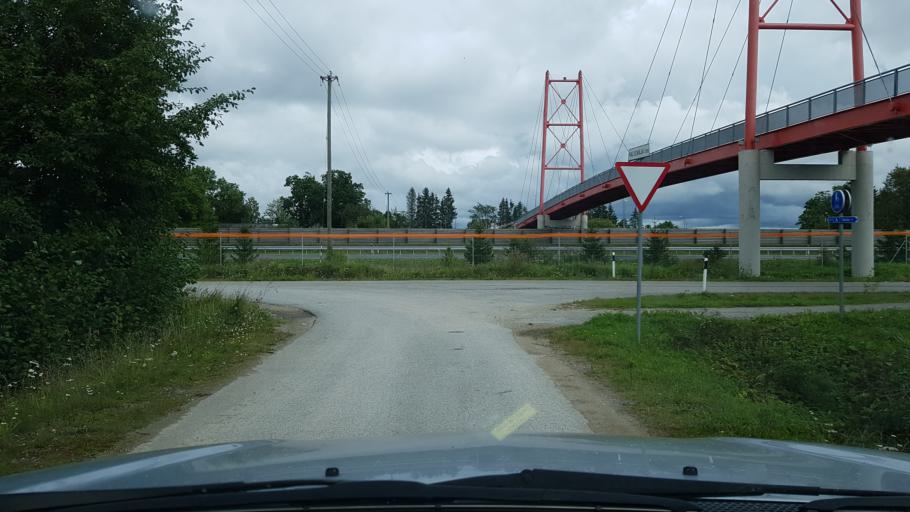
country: EE
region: Harju
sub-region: Rae vald
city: Vaida
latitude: 59.2803
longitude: 24.9773
